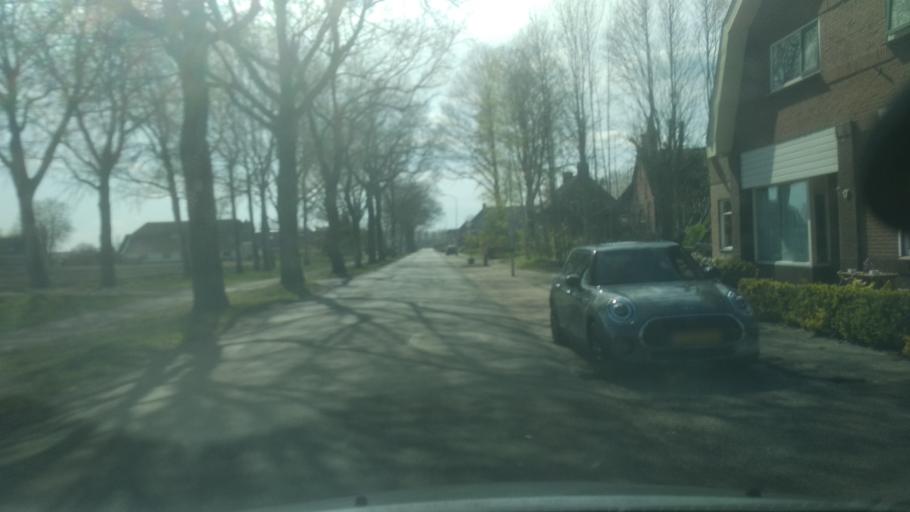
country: NL
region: Groningen
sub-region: Gemeente Stadskanaal
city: Stadskanaal
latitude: 52.9372
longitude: 6.8868
